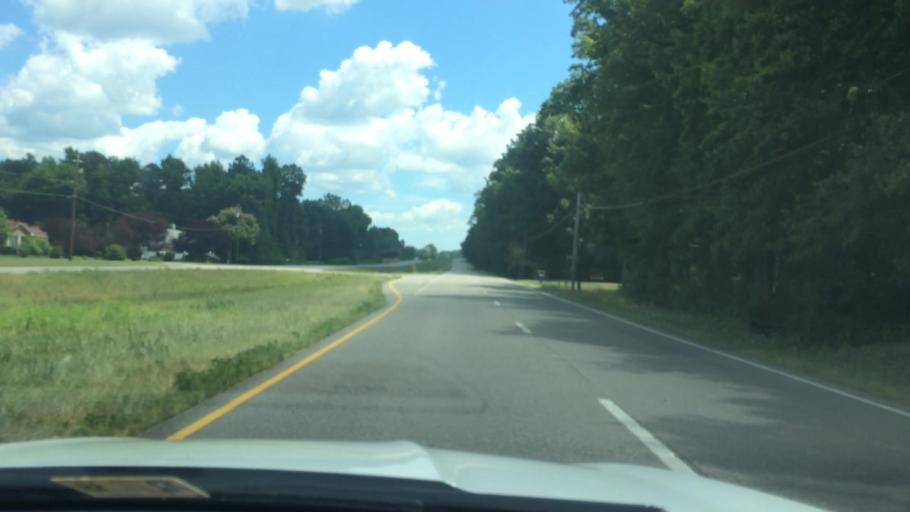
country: US
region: Virginia
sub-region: King William County
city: West Point
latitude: 37.5445
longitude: -76.7454
